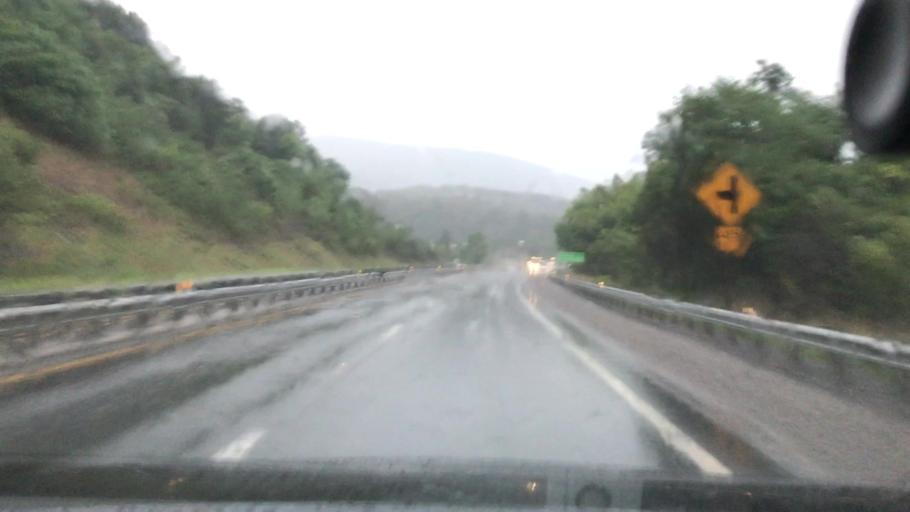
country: US
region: Virginia
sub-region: Giles County
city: Narrows
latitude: 37.3851
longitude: -80.8266
